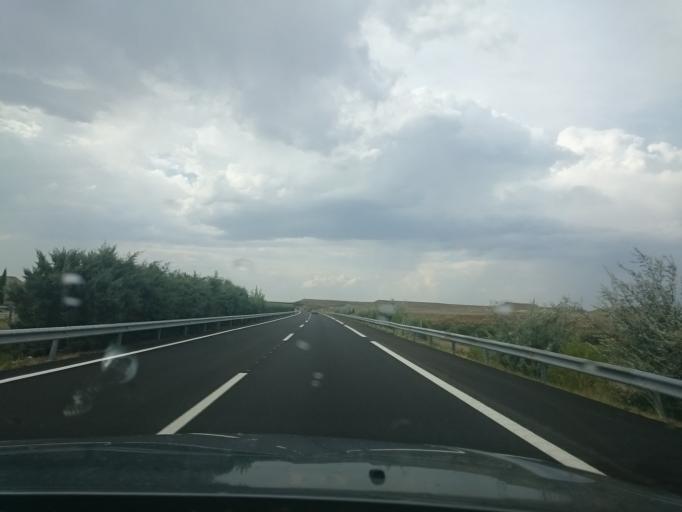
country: ES
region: La Rioja
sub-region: Provincia de La Rioja
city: Rincon de Soto
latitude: 42.1915
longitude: -1.8445
